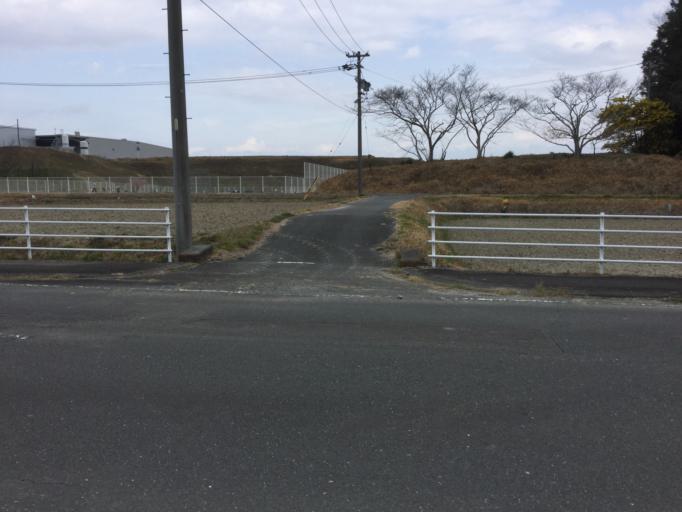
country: JP
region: Shizuoka
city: Kakegawa
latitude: 34.7022
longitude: 138.0352
